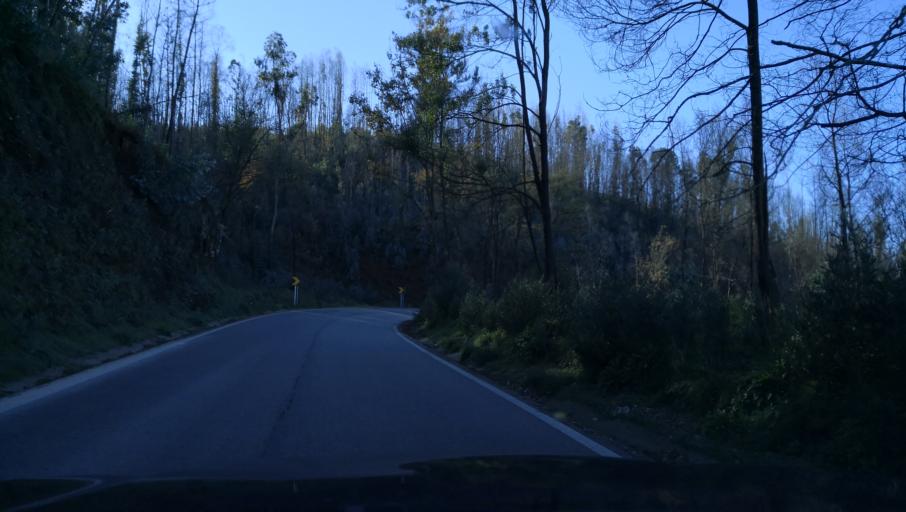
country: PT
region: Viseu
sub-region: Vouzela
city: Vouzela
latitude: 40.7295
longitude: -8.1385
